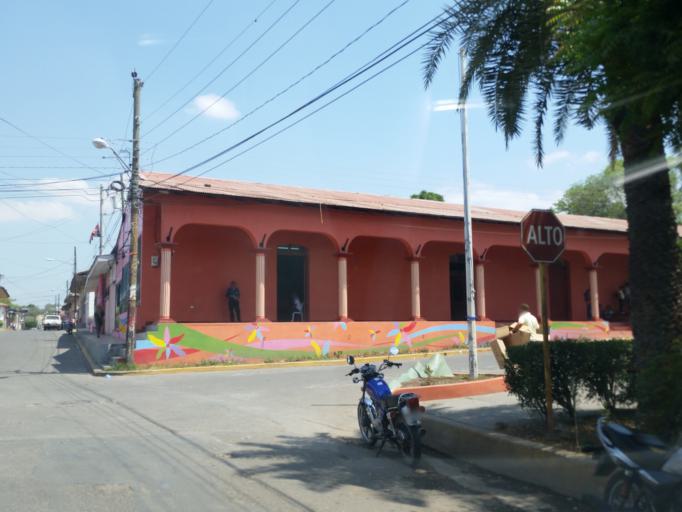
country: NI
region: Matagalpa
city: Ciudad Dario
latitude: 12.7279
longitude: -86.1238
